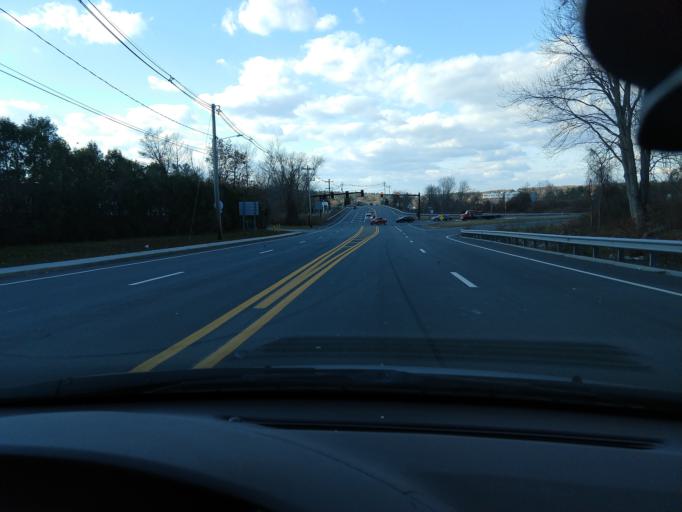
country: US
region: Massachusetts
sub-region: Middlesex County
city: Littleton Common
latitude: 42.5474
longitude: -71.4746
